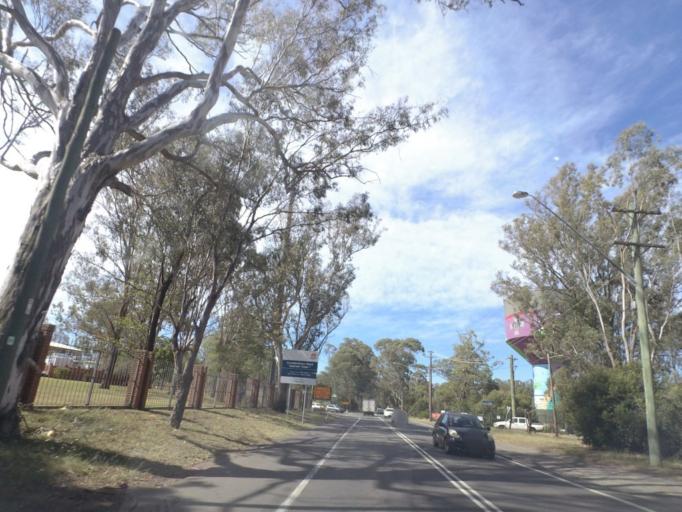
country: AU
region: New South Wales
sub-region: Campbelltown Municipality
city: Denham Court
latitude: -33.9788
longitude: 150.8498
